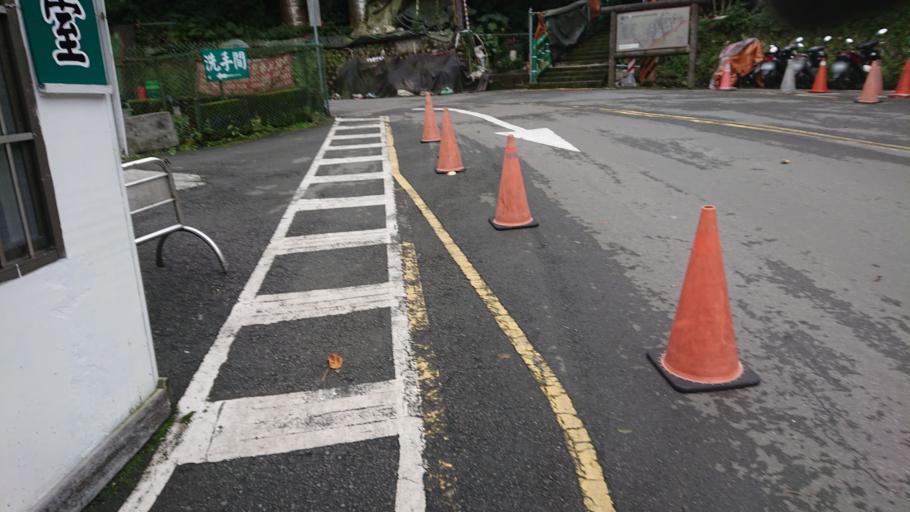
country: TW
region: Taipei
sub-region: Taipei
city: Banqiao
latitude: 24.9497
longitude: 121.4466
